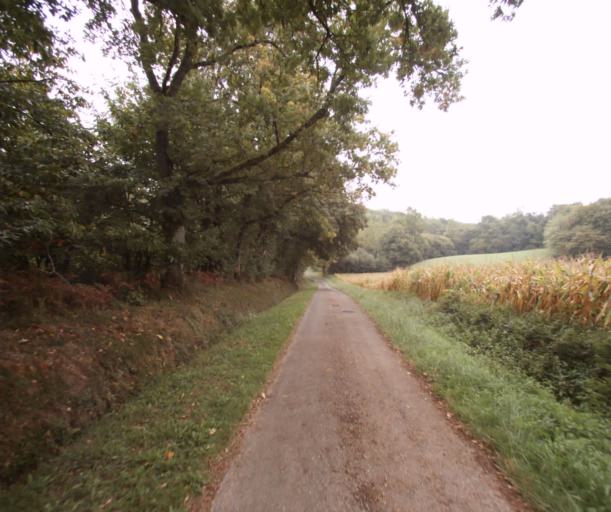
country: FR
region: Midi-Pyrenees
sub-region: Departement du Gers
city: Cazaubon
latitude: 43.9271
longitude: -0.1381
